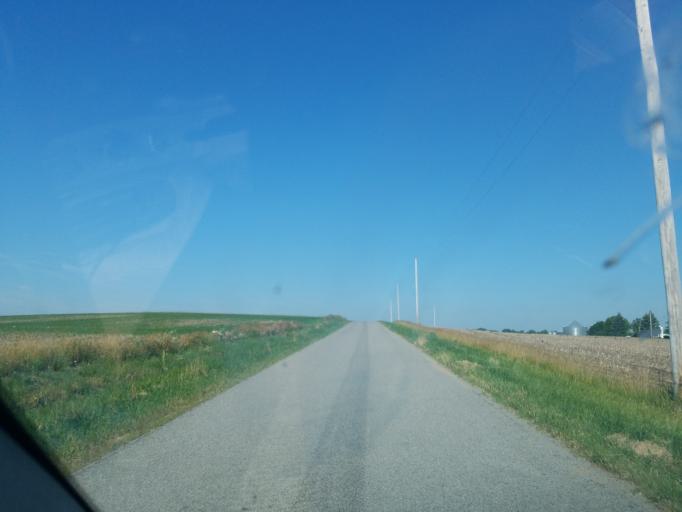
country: US
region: Ohio
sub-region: Logan County
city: Northwood
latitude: 40.4284
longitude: -83.6681
